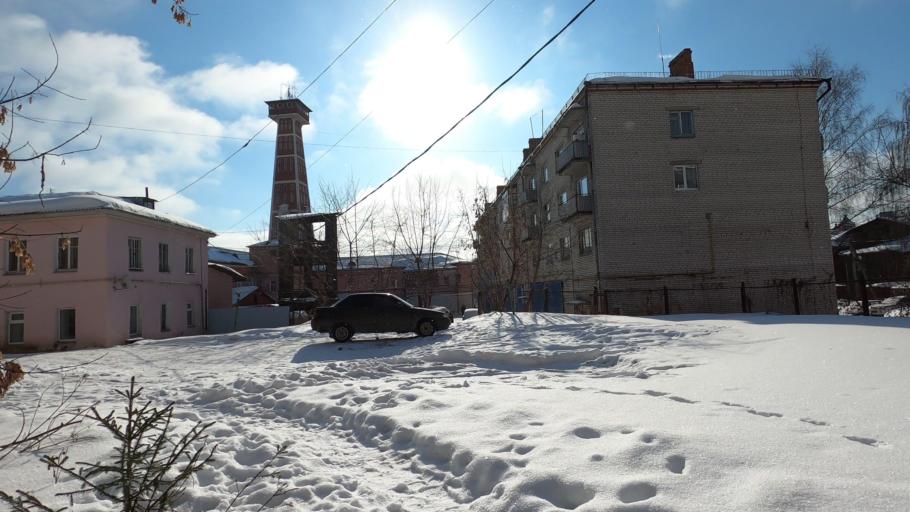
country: RU
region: Jaroslavl
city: Rybinsk
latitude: 58.0472
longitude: 38.8518
